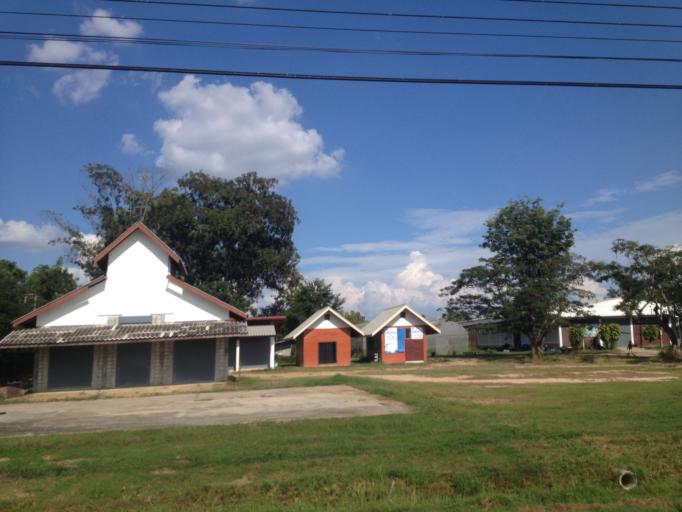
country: TH
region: Chiang Mai
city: Chiang Mai
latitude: 18.7641
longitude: 98.9307
